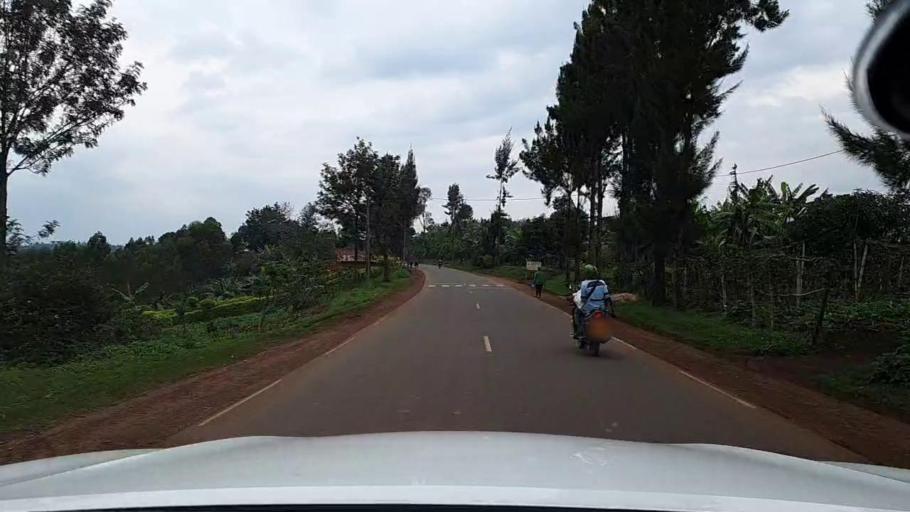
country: RW
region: Western Province
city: Cyangugu
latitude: -2.6081
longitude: 28.9350
